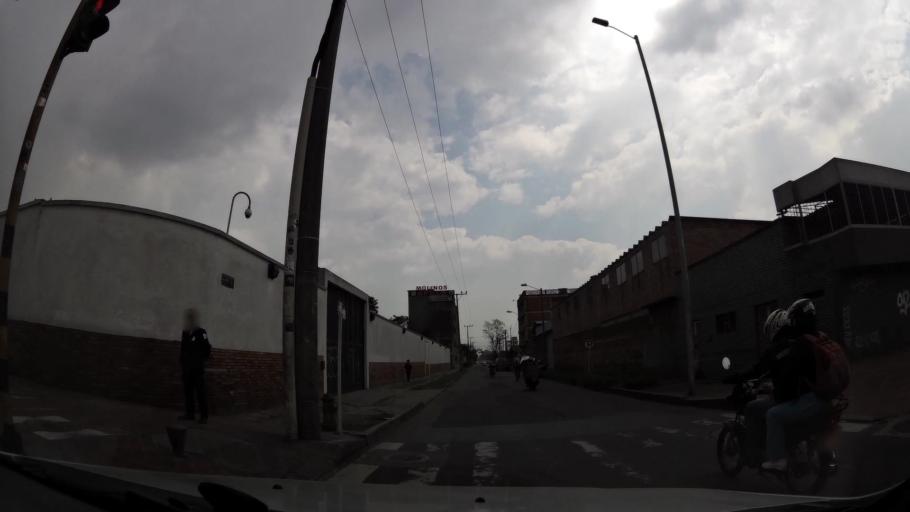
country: CO
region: Bogota D.C.
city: Bogota
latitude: 4.6185
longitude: -74.0969
